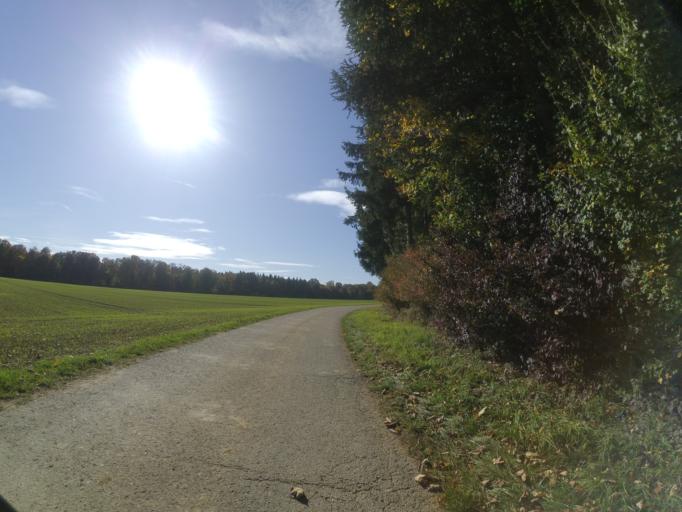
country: DE
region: Baden-Wuerttemberg
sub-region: Tuebingen Region
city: Weidenstetten
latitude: 48.5428
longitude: 9.9764
